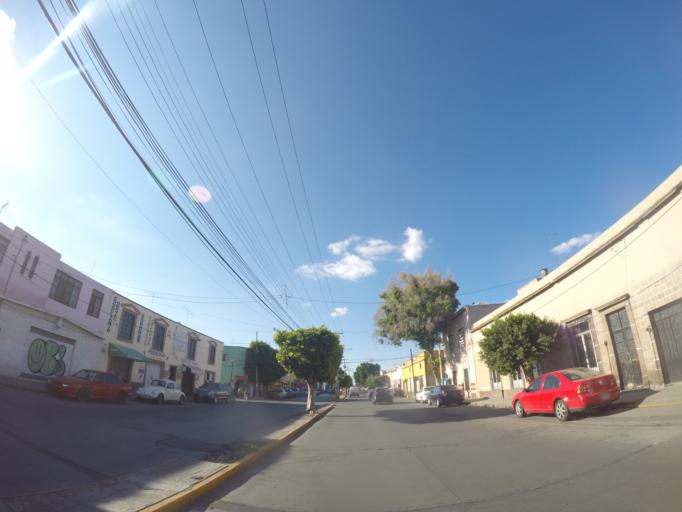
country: MX
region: San Luis Potosi
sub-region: San Luis Potosi
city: San Luis Potosi
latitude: 22.1583
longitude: -100.9797
